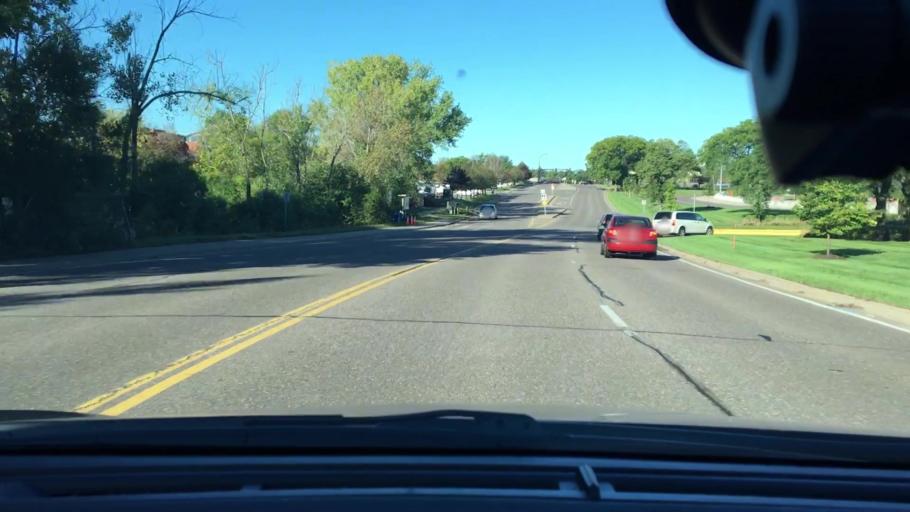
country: US
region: Minnesota
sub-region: Hennepin County
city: Minnetonka Mills
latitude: 44.9657
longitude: -93.4376
